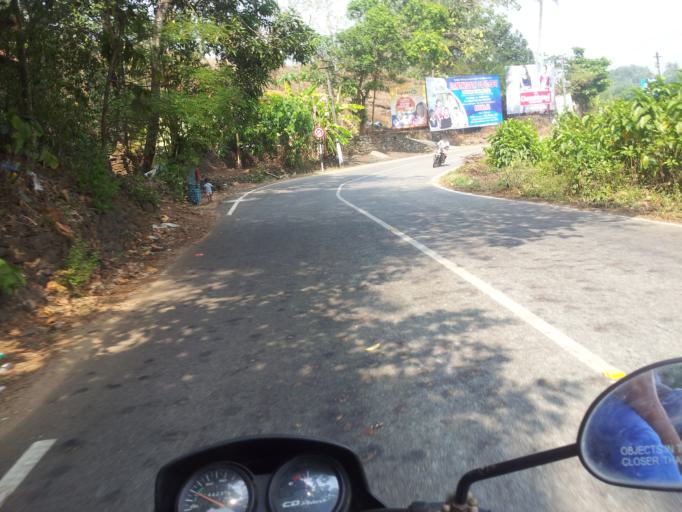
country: IN
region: Kerala
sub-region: Kottayam
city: Palackattumala
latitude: 9.8805
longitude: 76.6924
